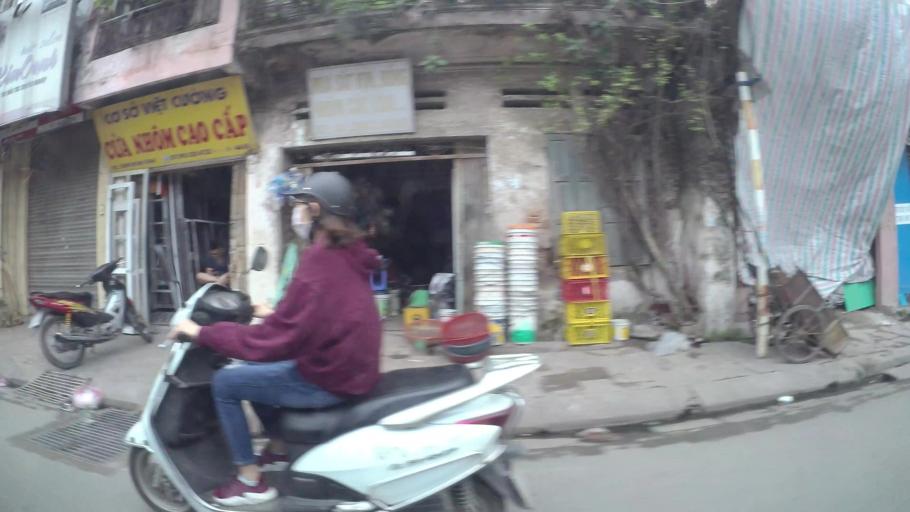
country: VN
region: Ha Noi
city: Hai BaTrung
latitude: 20.9953
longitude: 105.8583
